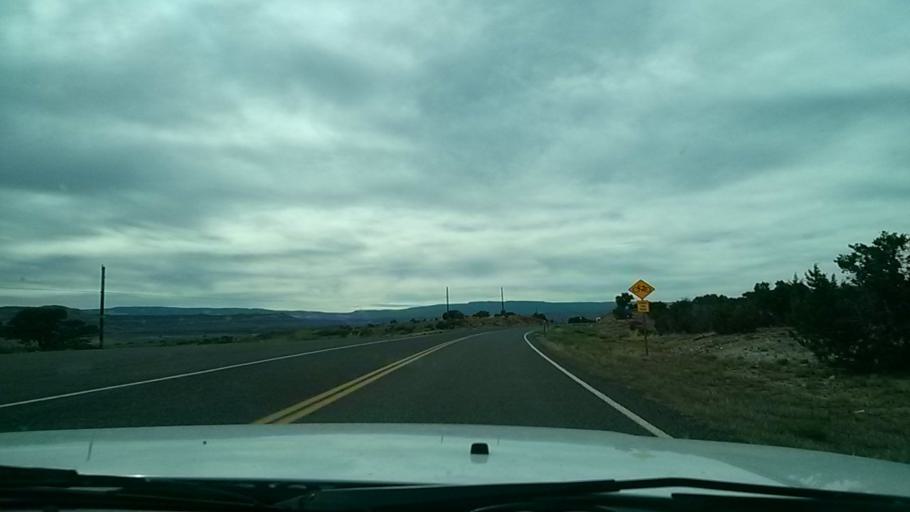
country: US
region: Utah
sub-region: Wayne County
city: Loa
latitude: 37.7277
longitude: -111.5314
